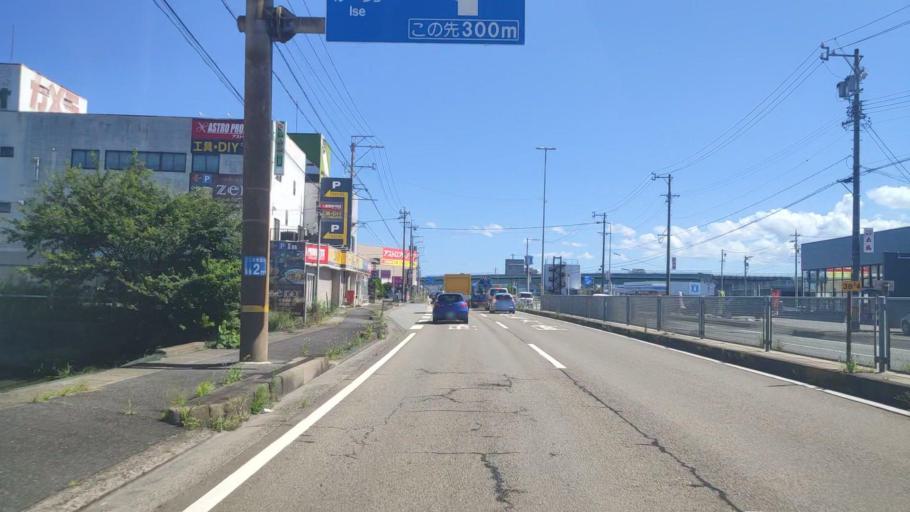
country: JP
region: Mie
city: Hisai-motomachi
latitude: 34.6185
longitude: 136.5156
